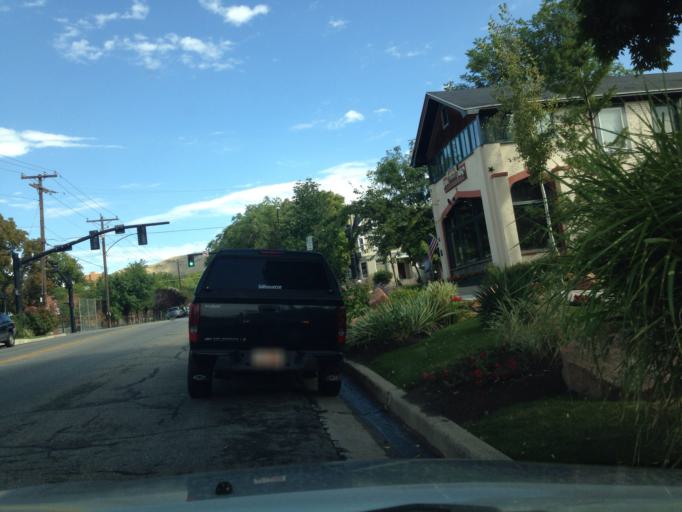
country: US
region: Utah
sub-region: Salt Lake County
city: Salt Lake City
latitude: 40.7712
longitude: -111.8775
